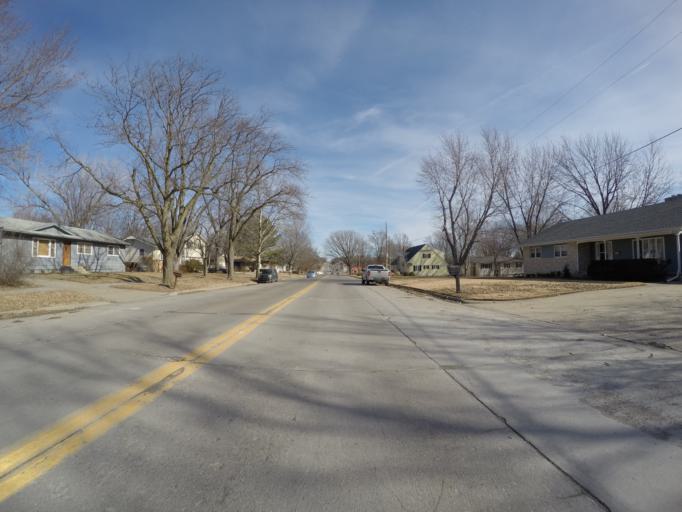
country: US
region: Kansas
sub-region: Riley County
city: Manhattan
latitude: 39.1928
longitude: -96.6148
